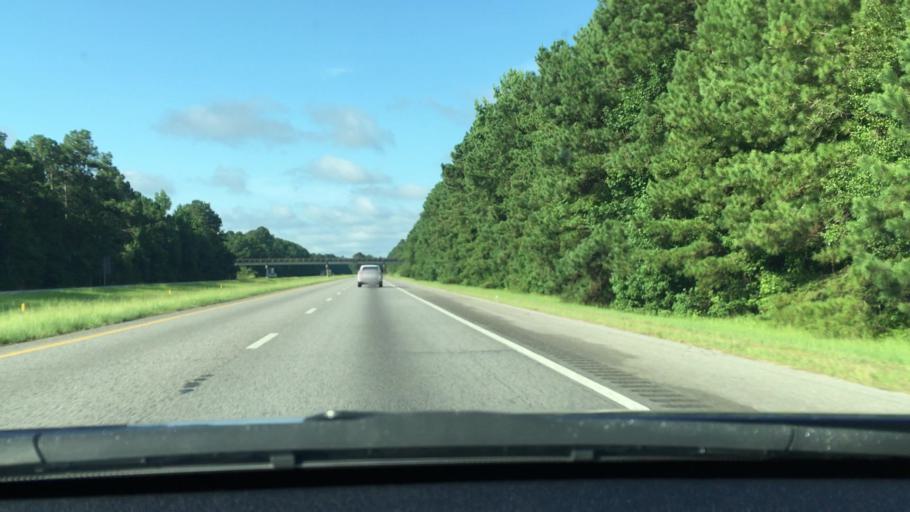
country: US
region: South Carolina
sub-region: Clarendon County
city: Manning
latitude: 33.6903
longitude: -80.2562
